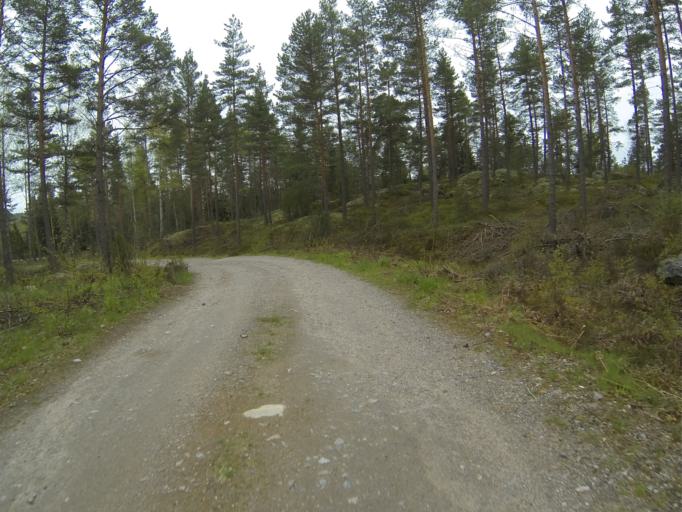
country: FI
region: Varsinais-Suomi
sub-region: Salo
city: Pertteli
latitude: 60.3831
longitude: 23.2171
